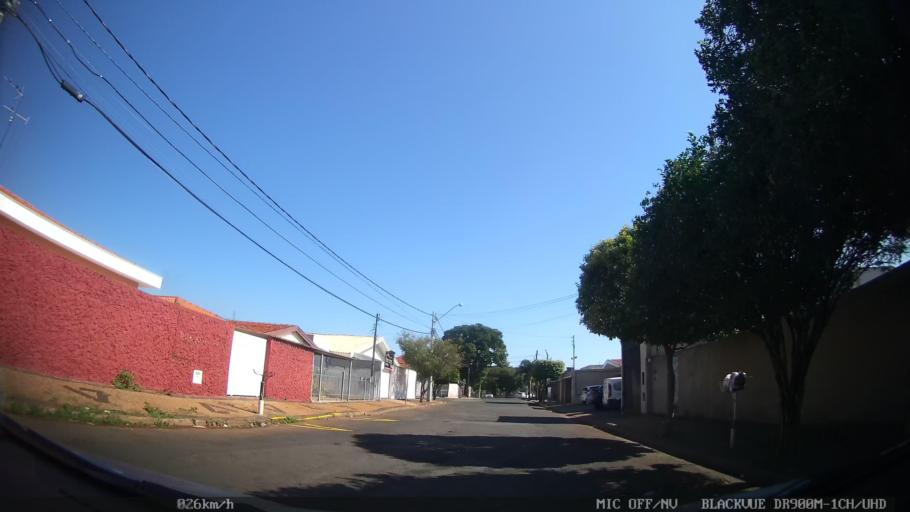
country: BR
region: Sao Paulo
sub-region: Americana
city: Americana
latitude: -22.7567
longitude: -47.3363
